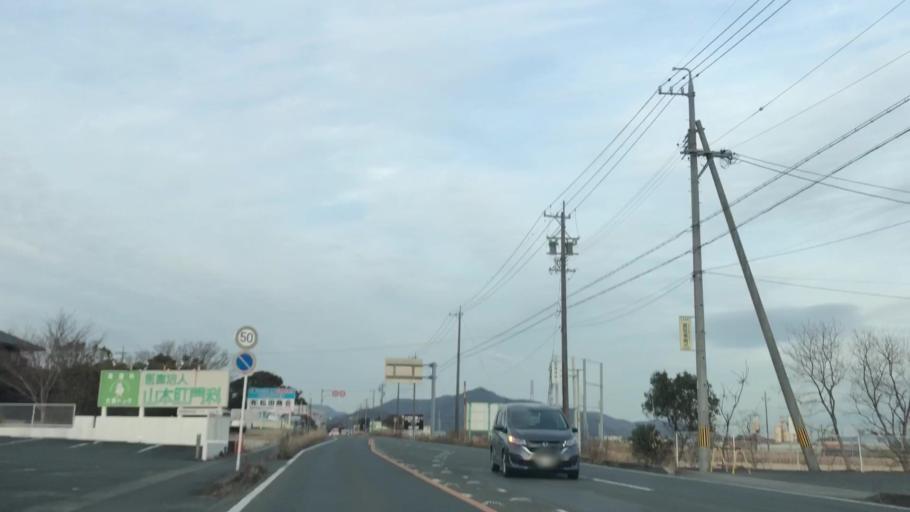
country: JP
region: Aichi
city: Toyohashi
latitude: 34.7170
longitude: 137.4059
